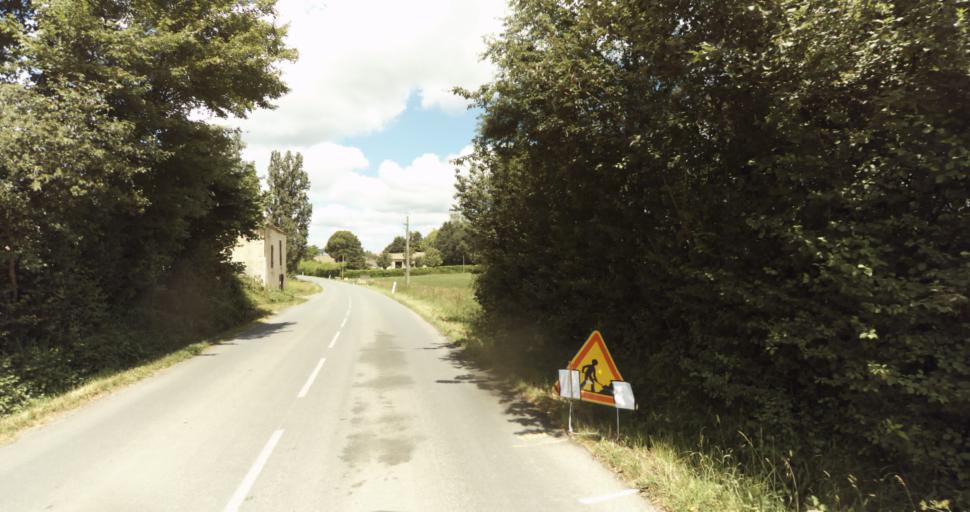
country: FR
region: Aquitaine
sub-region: Departement du Lot-et-Garonne
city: Villereal
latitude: 44.6967
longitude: 0.7510
